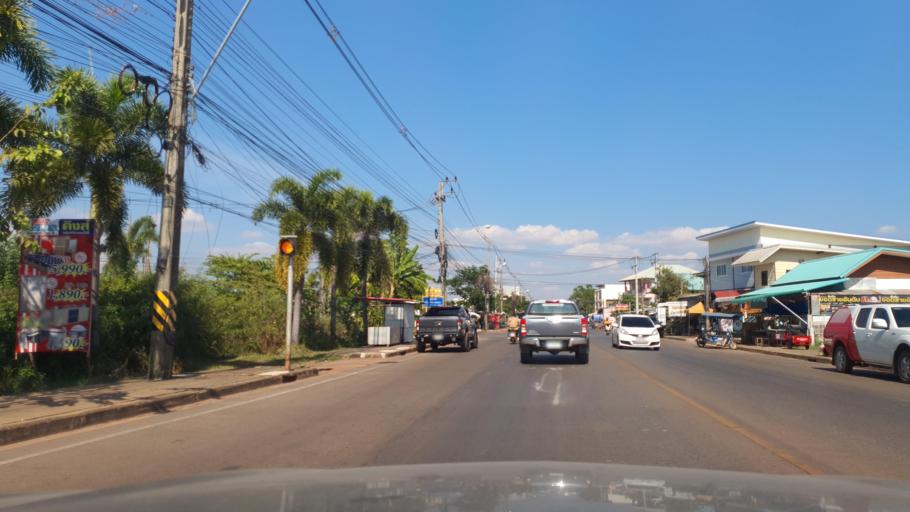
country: TH
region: Sakon Nakhon
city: Sakon Nakhon
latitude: 17.1714
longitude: 104.1260
